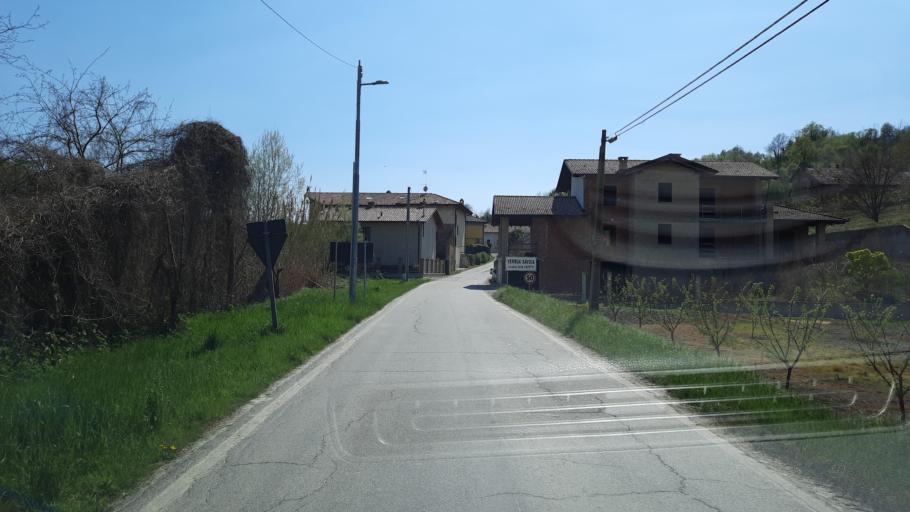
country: IT
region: Piedmont
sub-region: Provincia di Alessandria
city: Moncestino
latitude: 45.1599
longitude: 8.1322
